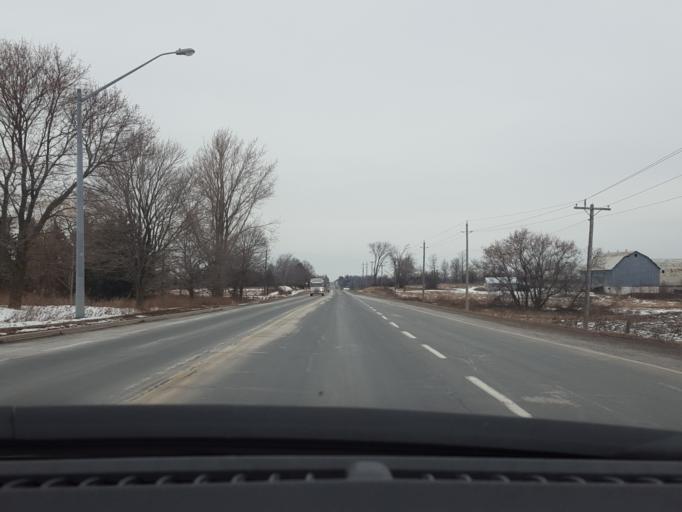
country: CA
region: Ontario
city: Newmarket
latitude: 44.1115
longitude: -79.4178
